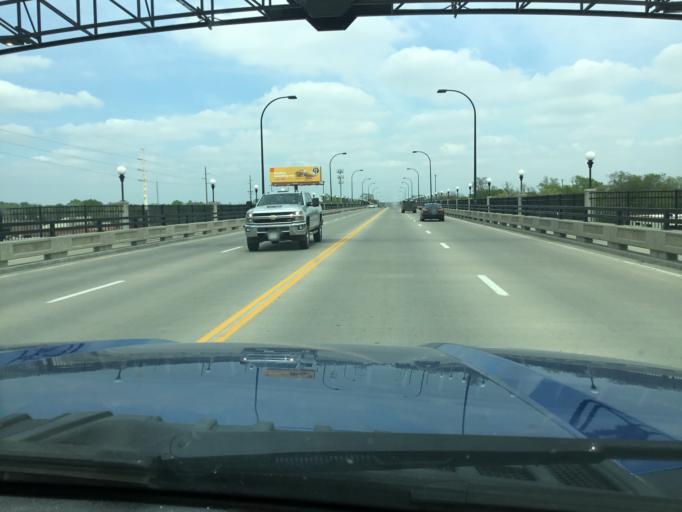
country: US
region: Kansas
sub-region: Shawnee County
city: Topeka
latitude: 39.0649
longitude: -95.6739
